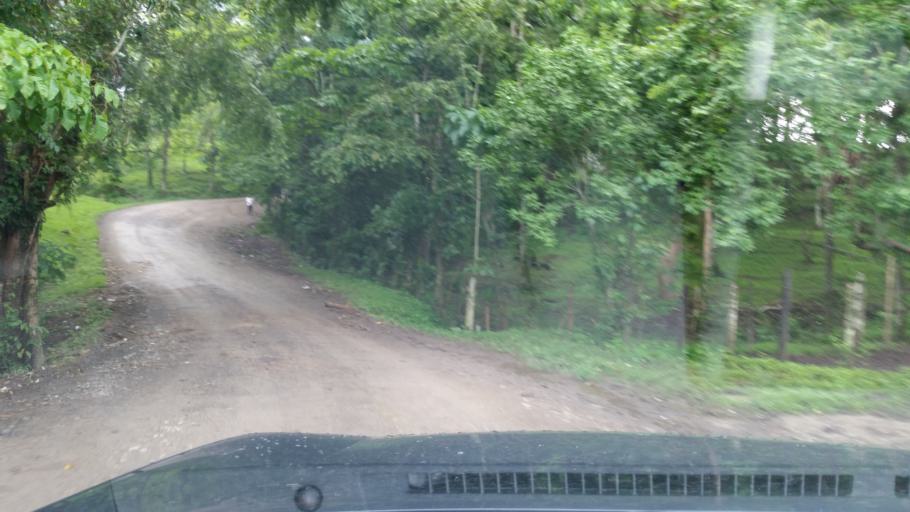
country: NI
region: Matagalpa
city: San Ramon
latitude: 13.0629
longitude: -85.7503
